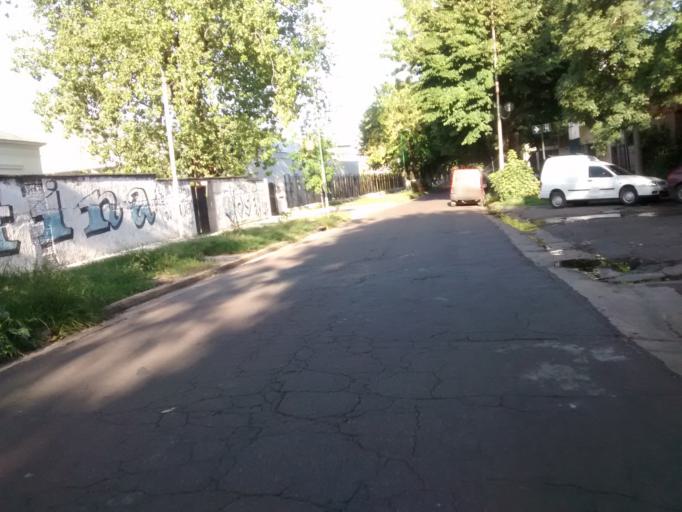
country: AR
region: Buenos Aires
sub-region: Partido de La Plata
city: La Plata
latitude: -34.9128
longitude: -57.9288
